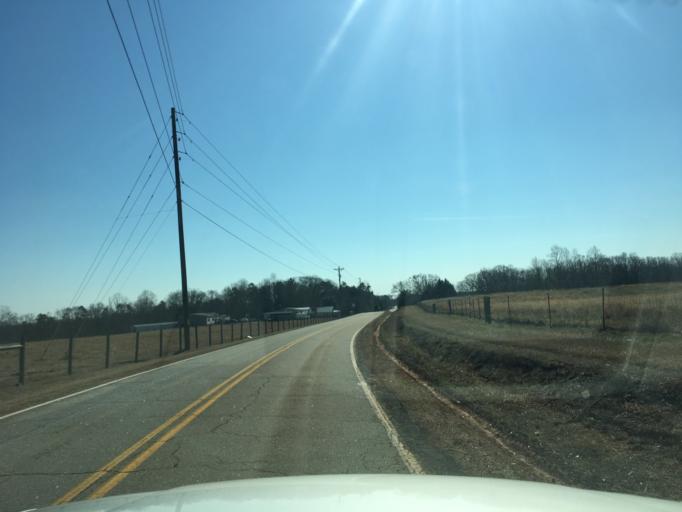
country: US
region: South Carolina
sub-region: Pickens County
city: Liberty
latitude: 34.8134
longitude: -82.7678
